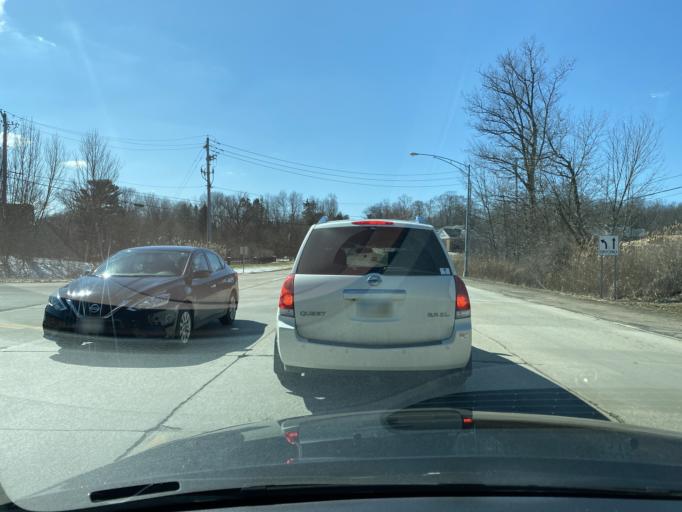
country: US
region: Ohio
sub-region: Summit County
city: Fairlawn
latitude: 41.1191
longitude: -81.6393
